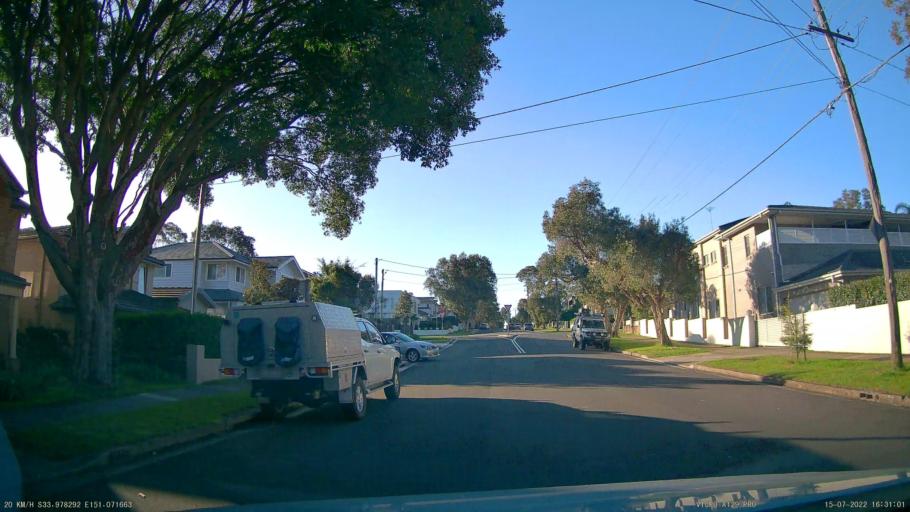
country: AU
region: New South Wales
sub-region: Hurstville
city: Oatley
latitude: -33.9781
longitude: 151.0717
